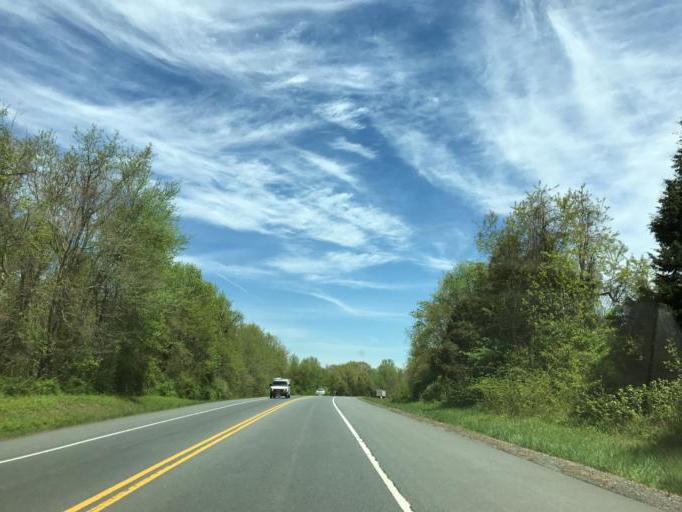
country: US
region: Maryland
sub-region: Cecil County
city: Elkton
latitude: 39.6161
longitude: -75.8443
